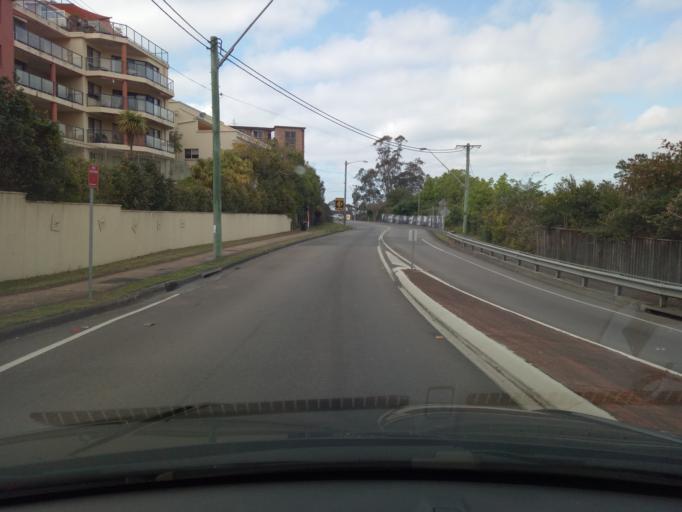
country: AU
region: New South Wales
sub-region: Gosford Shire
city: Gosford
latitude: -33.4295
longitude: 151.3426
